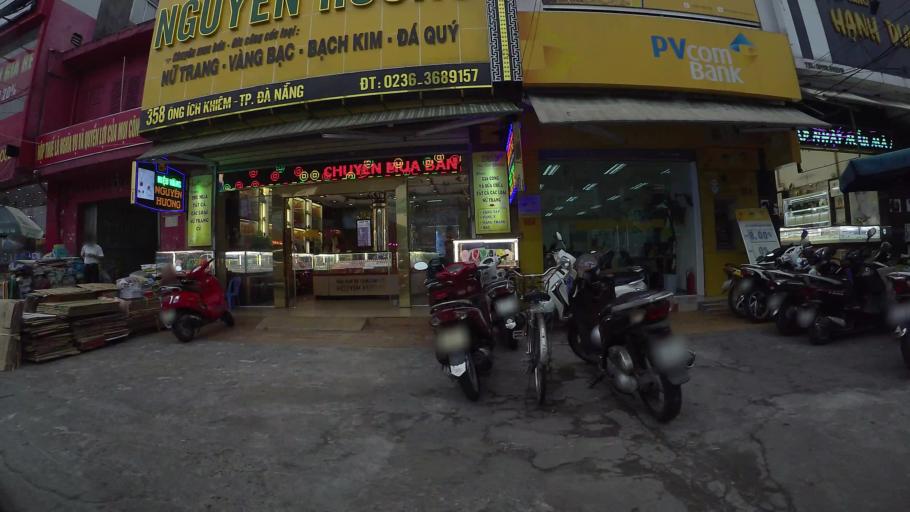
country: VN
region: Da Nang
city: Da Nang
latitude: 16.0677
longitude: 108.2140
